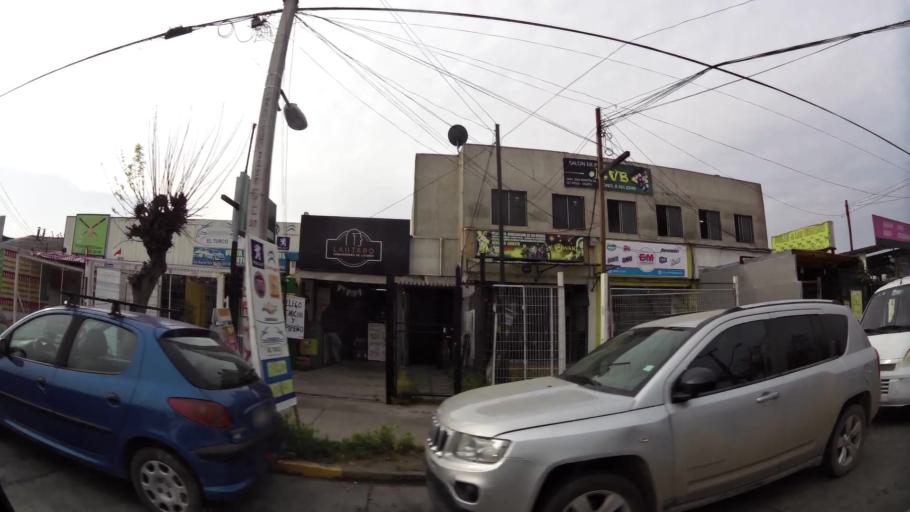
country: CL
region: Santiago Metropolitan
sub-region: Provincia de Santiago
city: Lo Prado
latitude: -33.5253
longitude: -70.7638
